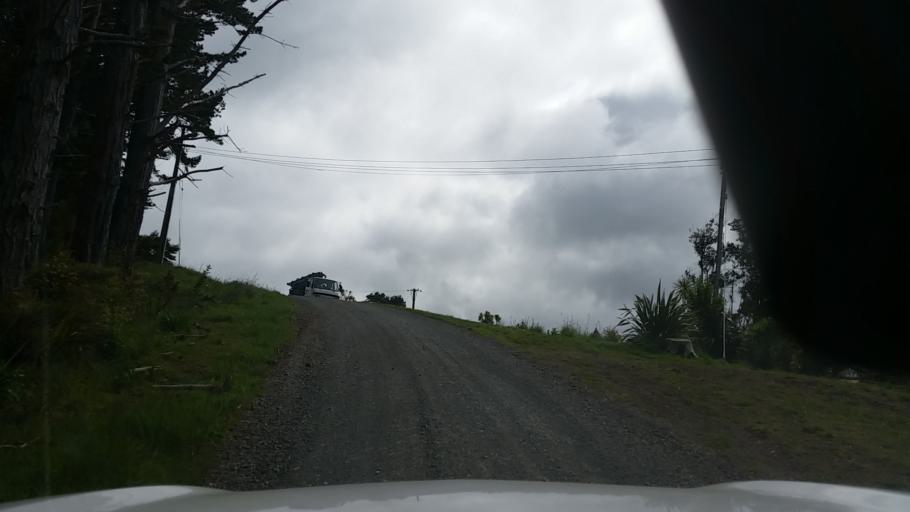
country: NZ
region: Auckland
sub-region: Auckland
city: Muriwai Beach
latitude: -36.8429
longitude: 174.5125
